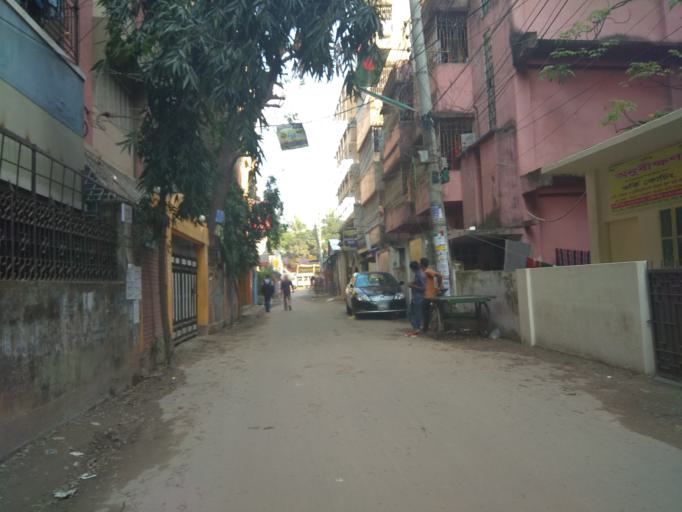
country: BD
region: Dhaka
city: Azimpur
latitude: 23.7618
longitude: 90.3582
